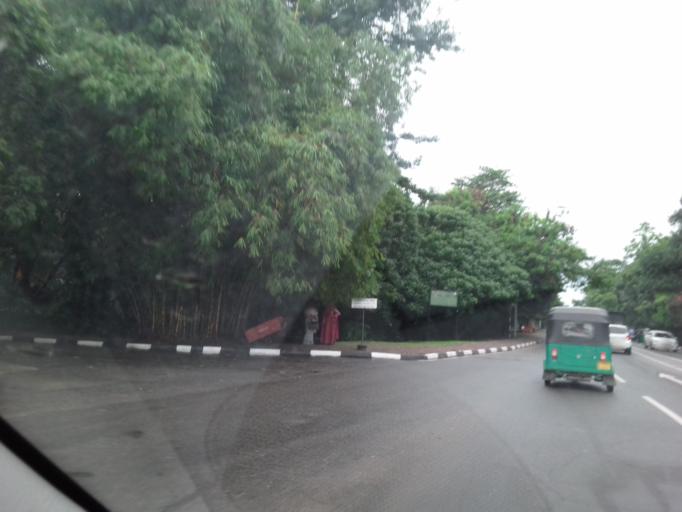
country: LK
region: Western
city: Battaramulla South
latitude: 6.9029
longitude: 79.9109
